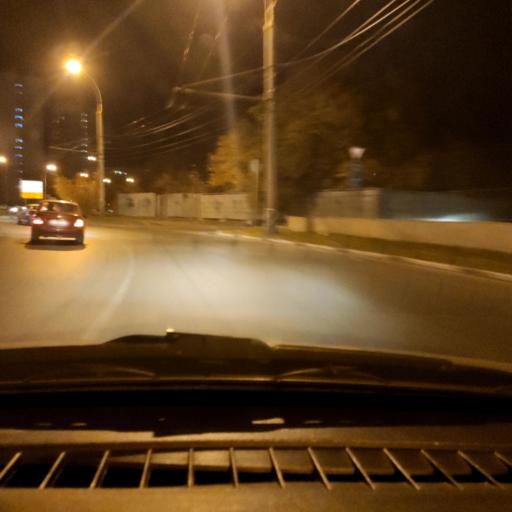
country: RU
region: Samara
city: Tol'yatti
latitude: 53.5243
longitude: 49.3275
